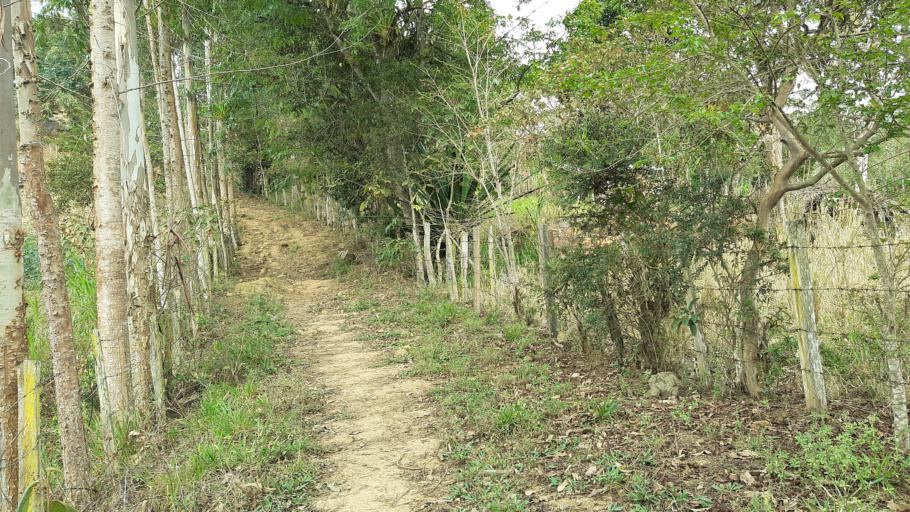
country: CO
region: Boyaca
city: Garagoa
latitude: 5.0878
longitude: -73.3589
